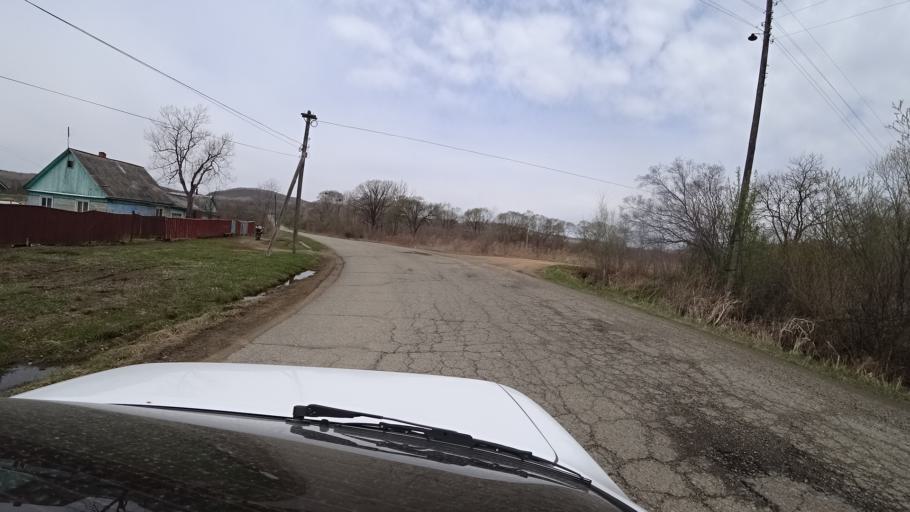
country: RU
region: Primorskiy
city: Dal'nerechensk
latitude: 45.7958
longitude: 134.1068
